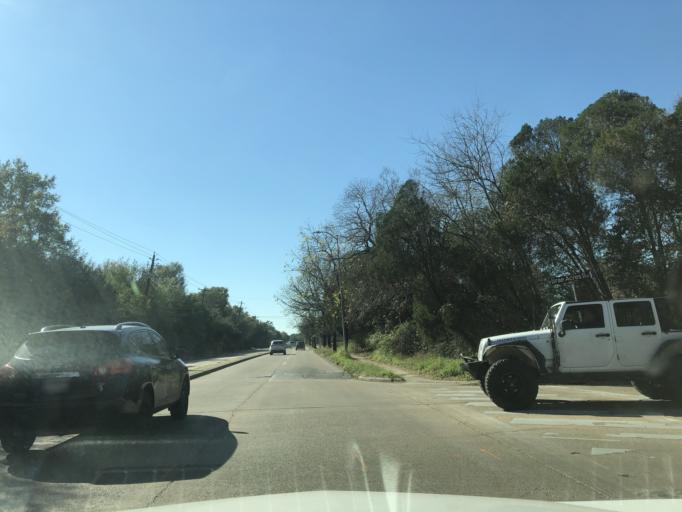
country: US
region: Texas
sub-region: Fort Bend County
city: Missouri City
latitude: 29.6804
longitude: -95.5216
